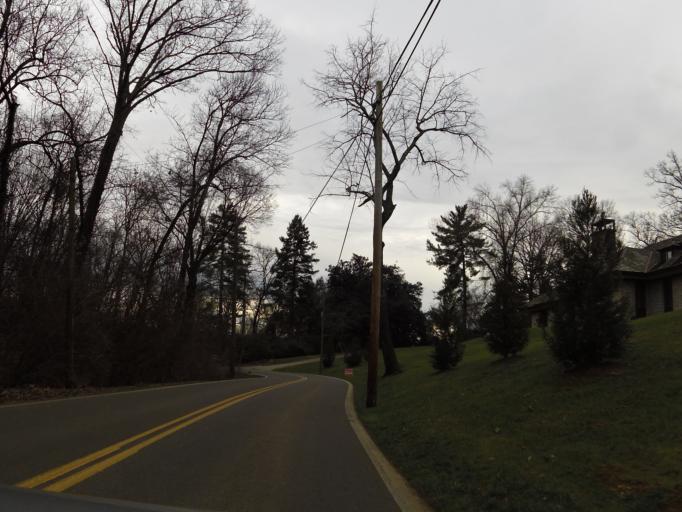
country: US
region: Tennessee
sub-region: Knox County
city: Knoxville
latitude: 35.9382
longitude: -83.9802
